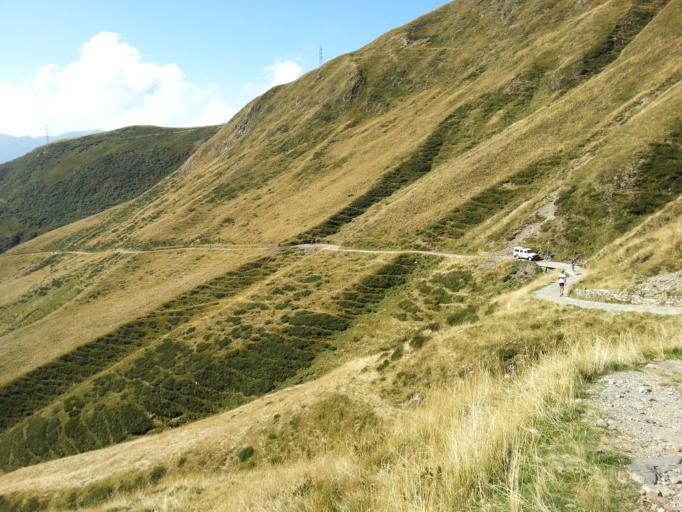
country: CH
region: Grisons
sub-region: Moesa District
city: Roveredo
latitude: 46.1662
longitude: 9.1629
